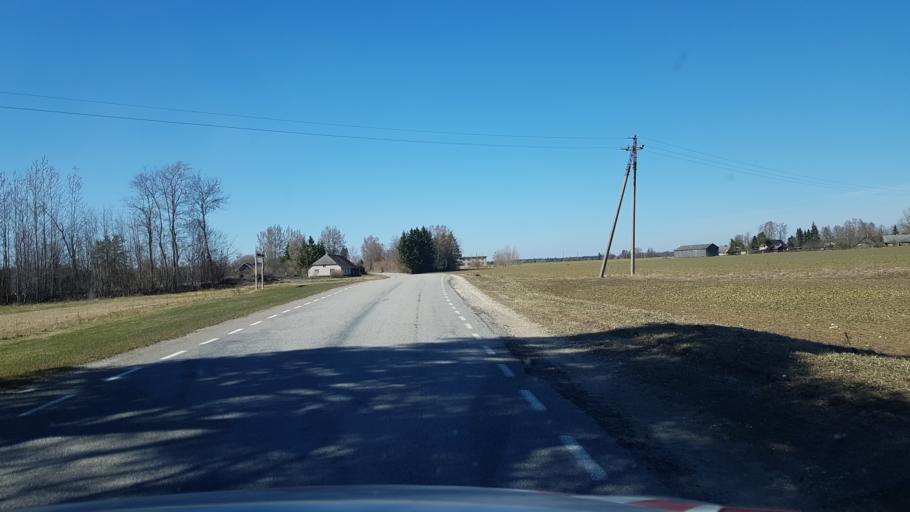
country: EE
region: Laeaene-Virumaa
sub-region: Vaeike-Maarja vald
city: Vaike-Maarja
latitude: 59.1097
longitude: 26.3768
